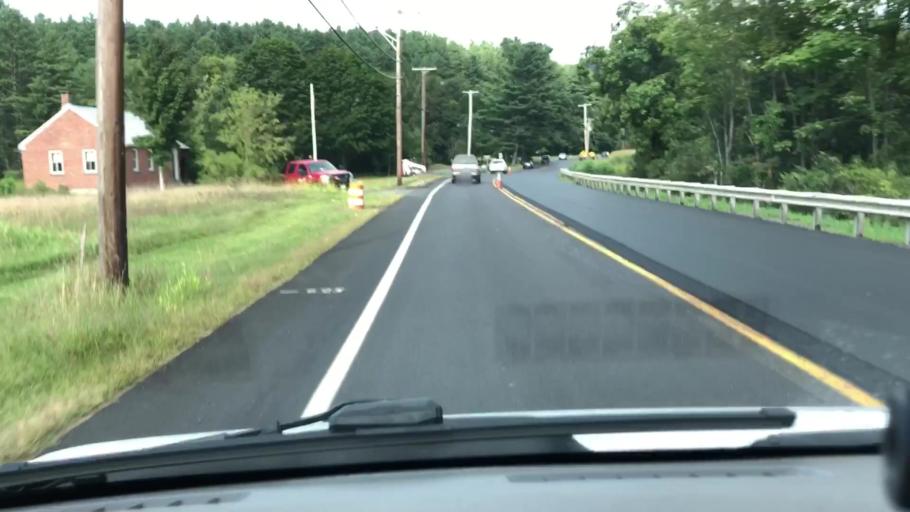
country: US
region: Massachusetts
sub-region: Franklin County
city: Buckland
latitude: 42.6230
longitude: -72.7873
